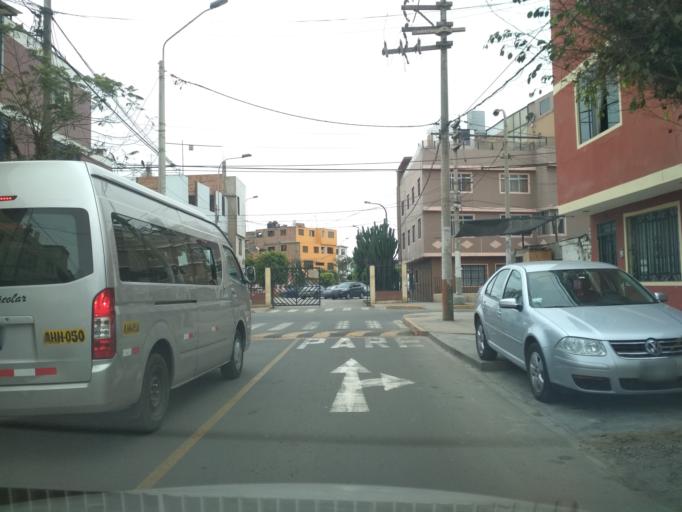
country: PE
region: Callao
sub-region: Callao
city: Callao
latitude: -12.0529
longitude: -77.1009
